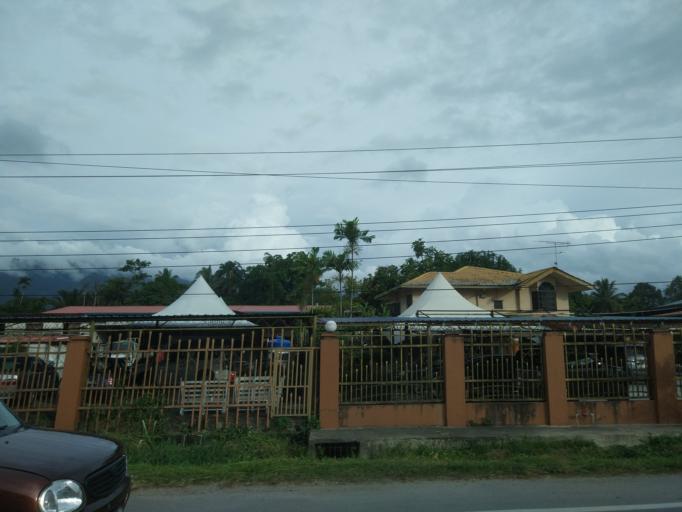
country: MY
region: Sabah
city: Kota Kinabalu
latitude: 6.0481
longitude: 116.1650
